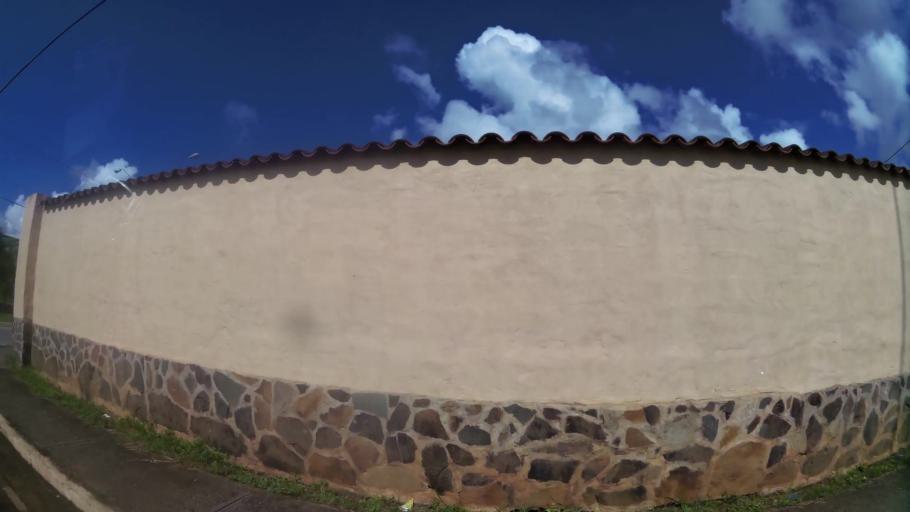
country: PA
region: Panama
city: Nuevo Arraijan
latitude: 8.9018
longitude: -79.7436
